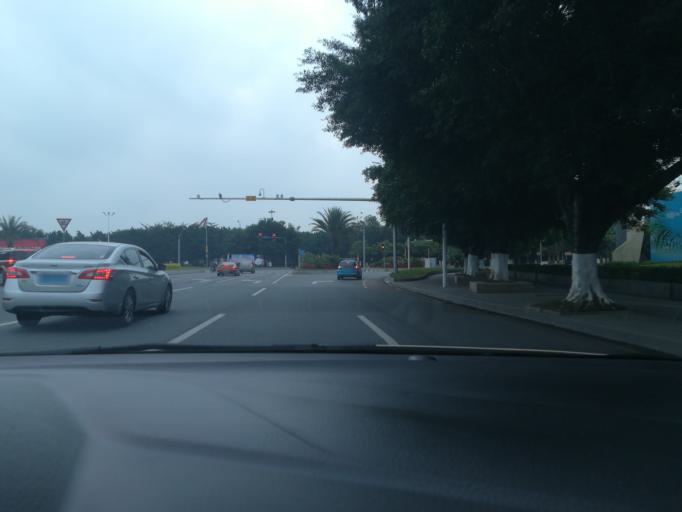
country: CN
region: Guangdong
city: Nansha
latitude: 22.8006
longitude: 113.5814
